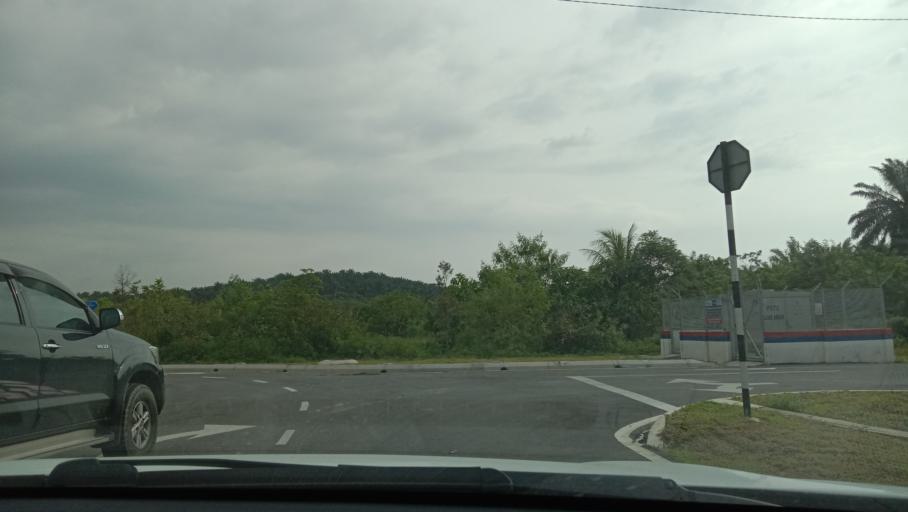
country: MY
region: Selangor
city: Ladang Seri Kundang
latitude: 3.2347
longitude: 101.4774
